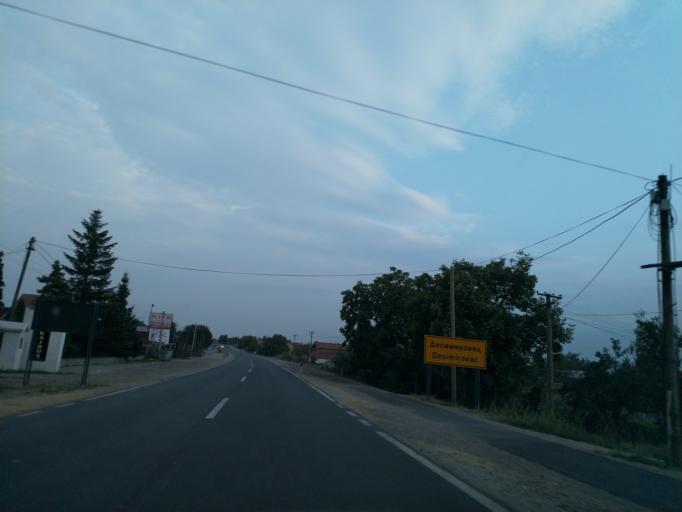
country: RS
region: Central Serbia
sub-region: Sumadijski Okrug
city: Kragujevac
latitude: 44.0847
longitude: 20.8675
